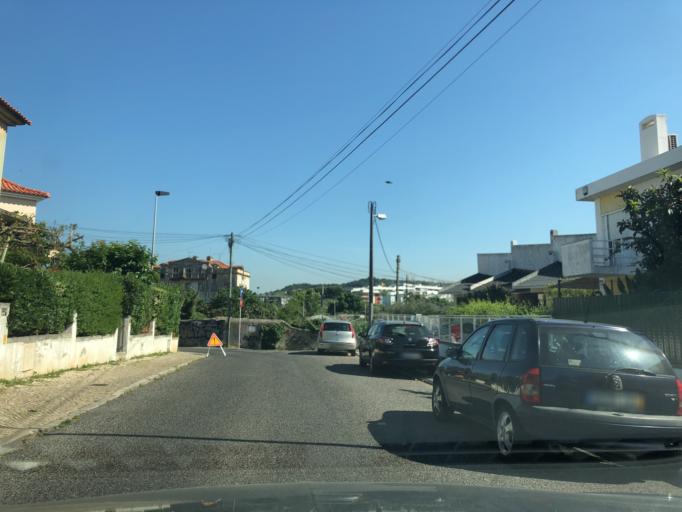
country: PT
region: Lisbon
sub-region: Oeiras
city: Terrugem
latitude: 38.7069
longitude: -9.2735
